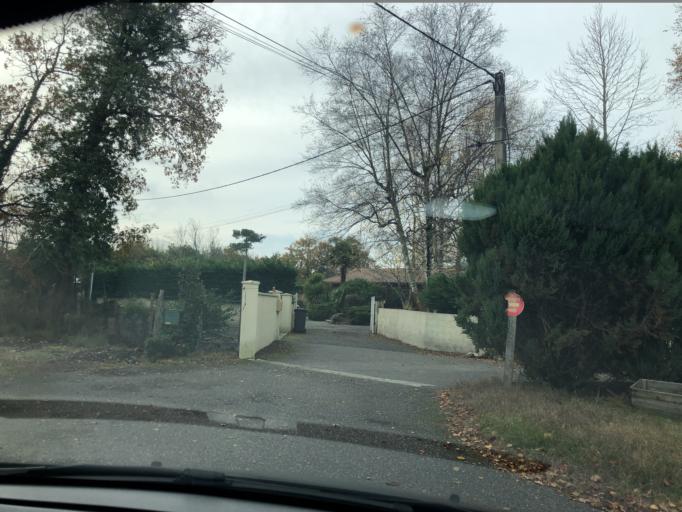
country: FR
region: Aquitaine
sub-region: Departement de la Gironde
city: Hourtin
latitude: 45.1870
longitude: -1.0685
